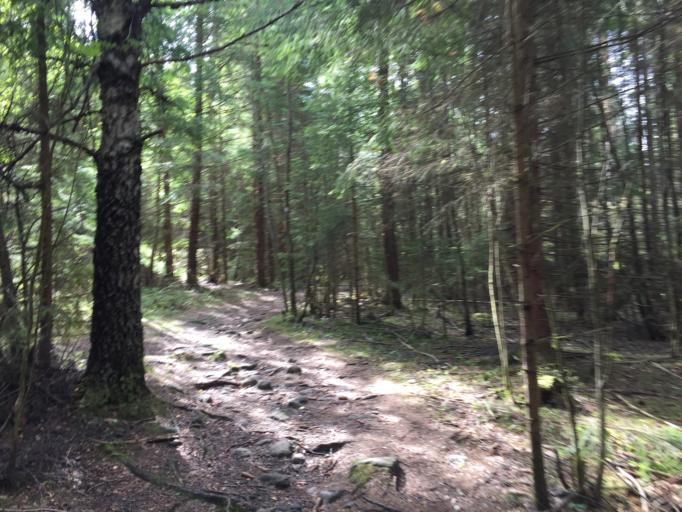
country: NO
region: Akershus
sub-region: Skedsmo
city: Lillestrom
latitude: 59.9229
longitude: 11.0125
